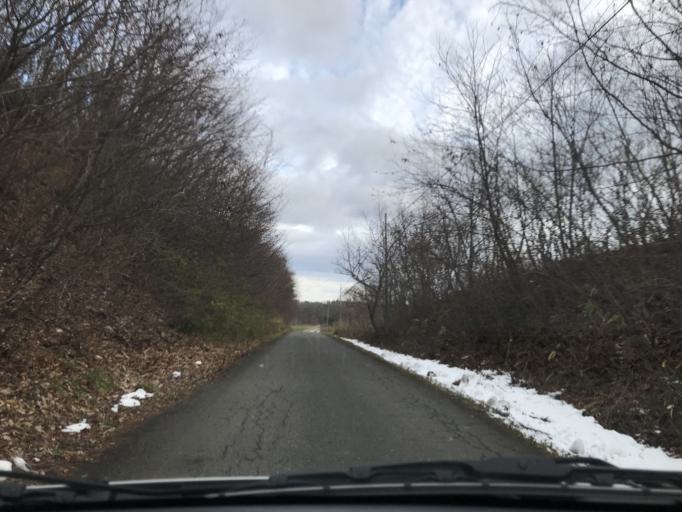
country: JP
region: Iwate
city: Ichinoseki
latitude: 38.9779
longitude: 141.0199
